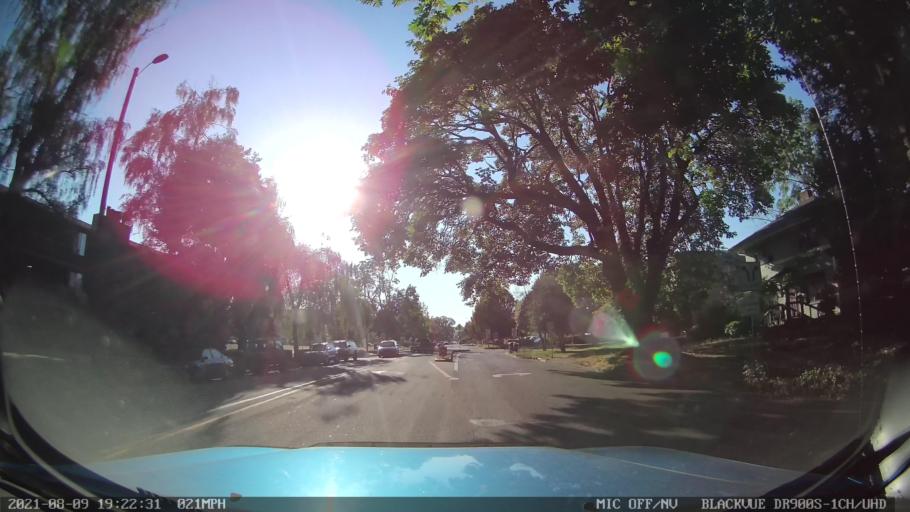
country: US
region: Oregon
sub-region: Marion County
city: Salem
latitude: 44.9398
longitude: -123.0233
